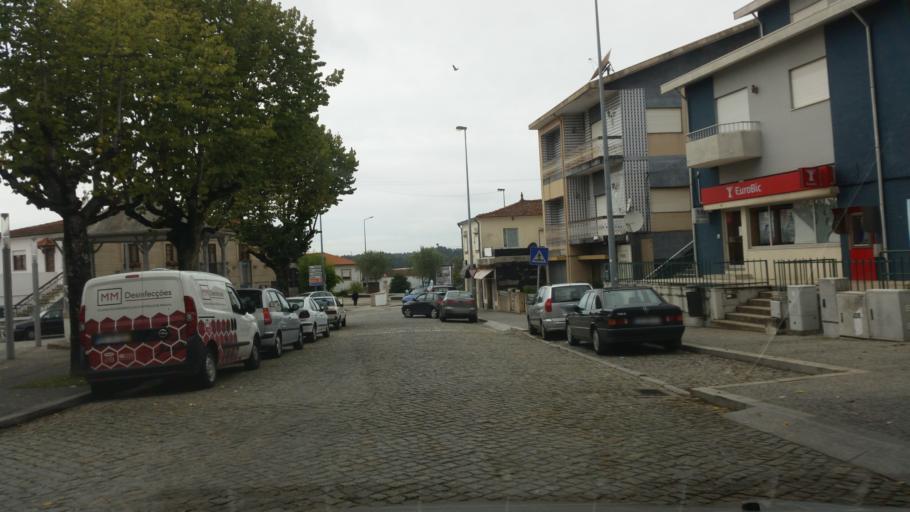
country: PT
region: Porto
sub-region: Valongo
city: Ermesinde
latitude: 41.2445
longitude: -8.5504
